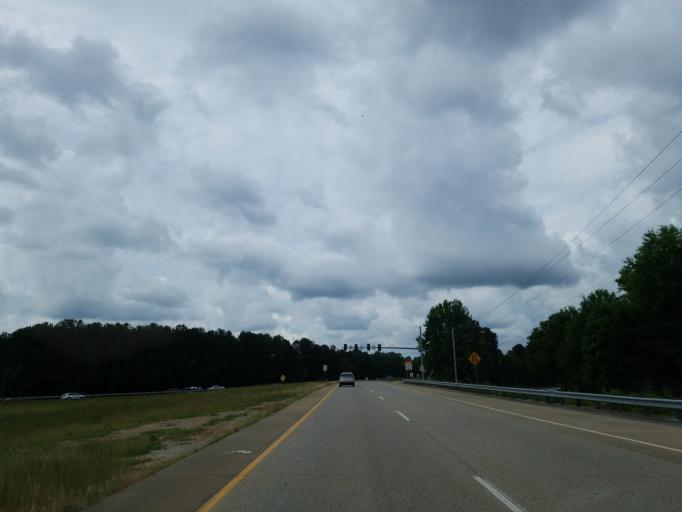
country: US
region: Georgia
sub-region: Fulton County
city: Milton
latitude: 34.1144
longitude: -84.2209
